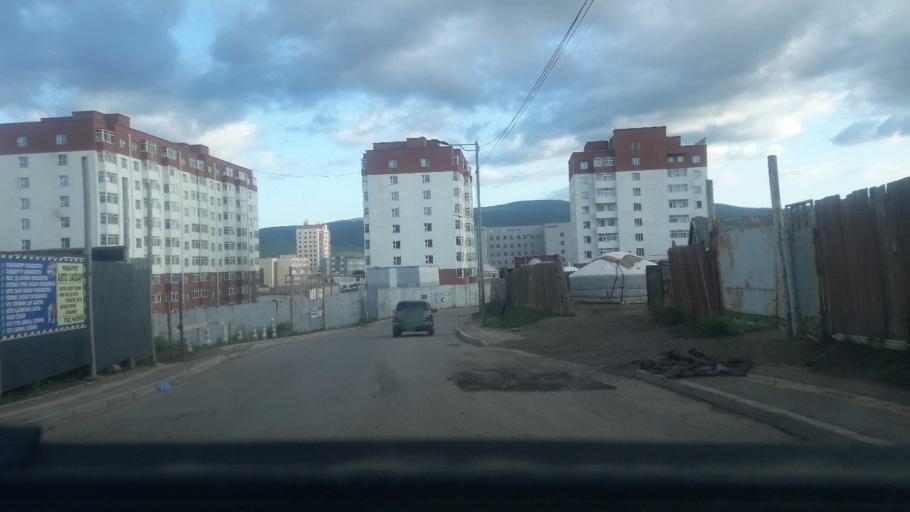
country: MN
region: Ulaanbaatar
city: Ulaanbaatar
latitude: 47.9185
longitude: 106.9954
